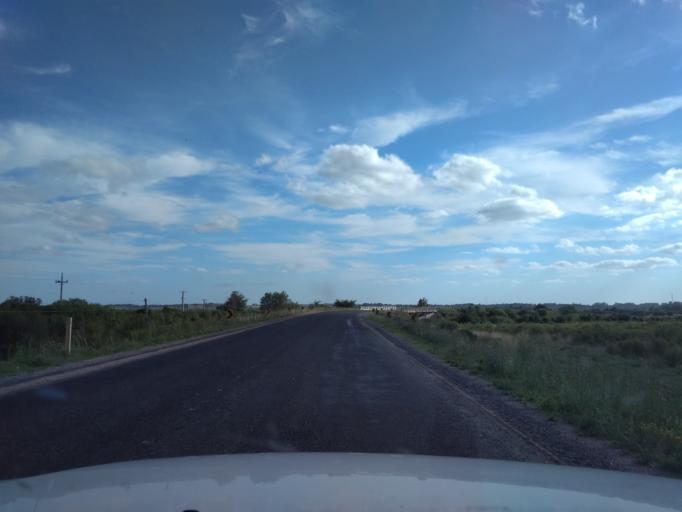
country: UY
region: Canelones
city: San Ramon
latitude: -34.2644
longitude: -55.9280
